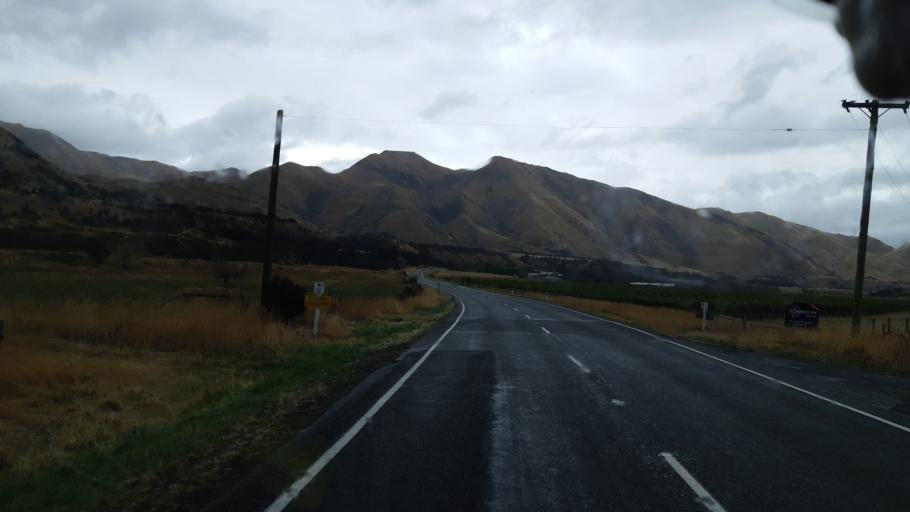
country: NZ
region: Canterbury
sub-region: Hurunui District
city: Amberley
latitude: -42.6254
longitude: 172.7661
